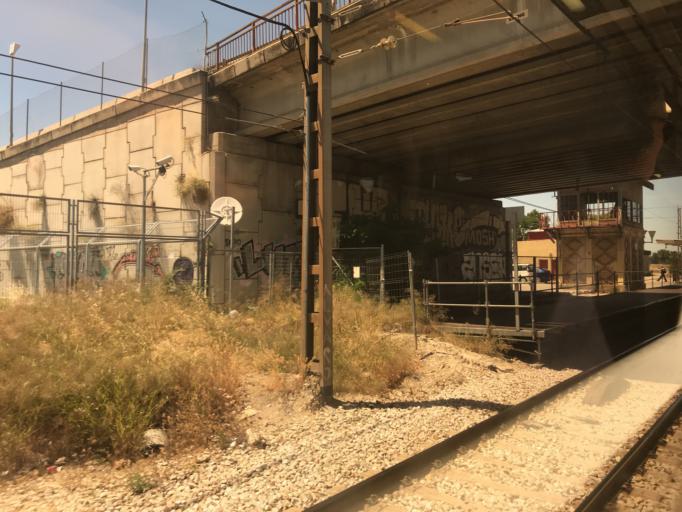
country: ES
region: Madrid
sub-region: Provincia de Madrid
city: Getafe
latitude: 40.3047
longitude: -3.7075
